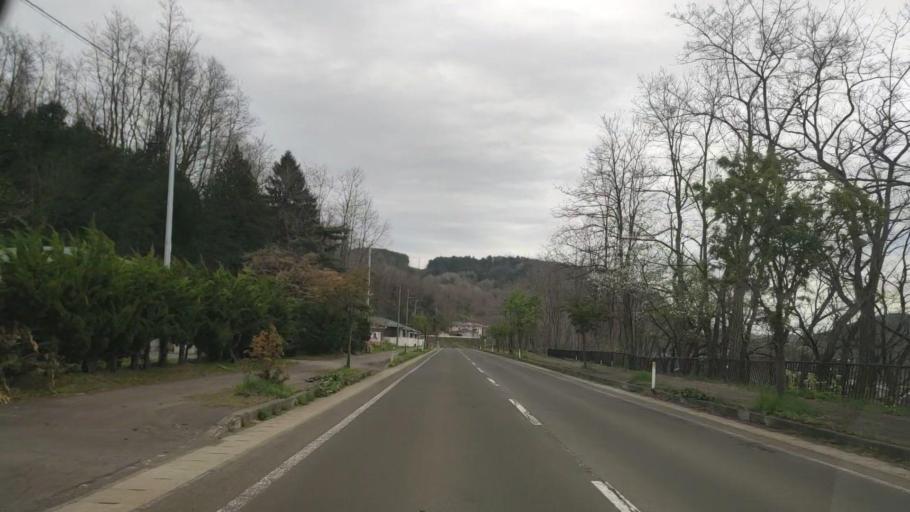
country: JP
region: Akita
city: Hanawa
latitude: 40.3286
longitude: 140.7472
